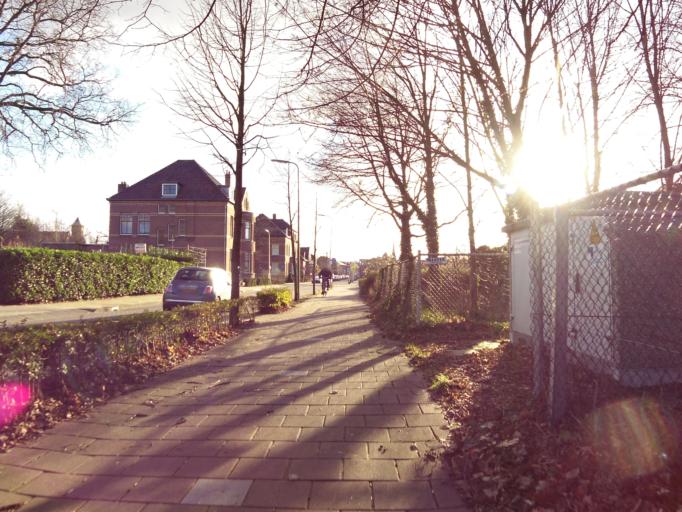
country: NL
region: South Holland
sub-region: Gemeente Noordwijkerhout
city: Noordwijkerhout
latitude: 52.2660
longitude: 4.4936
